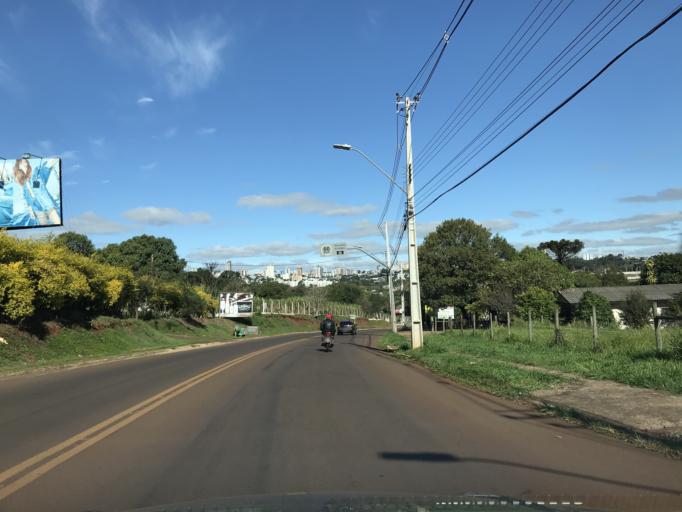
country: BR
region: Parana
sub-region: Cascavel
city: Cascavel
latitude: -24.9235
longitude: -53.4747
